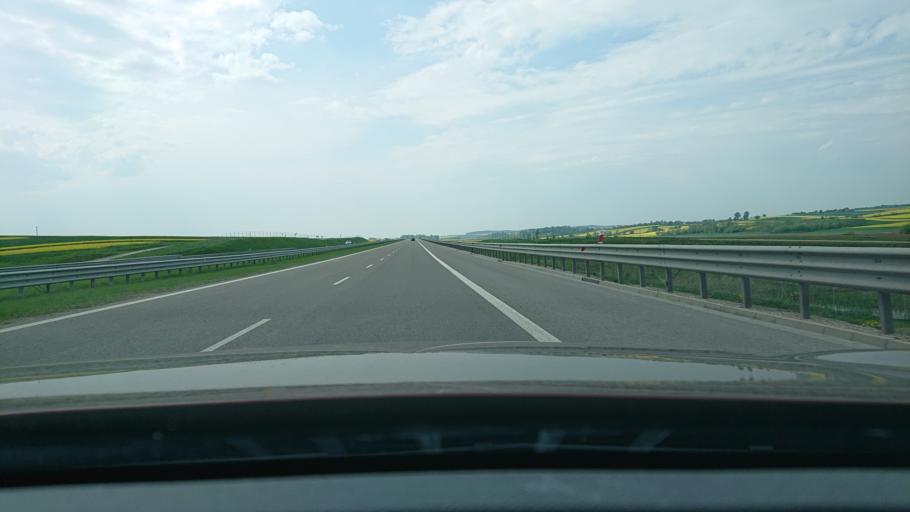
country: PL
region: Subcarpathian Voivodeship
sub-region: Powiat jaroslawski
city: Rokietnica
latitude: 49.9331
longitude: 22.7046
